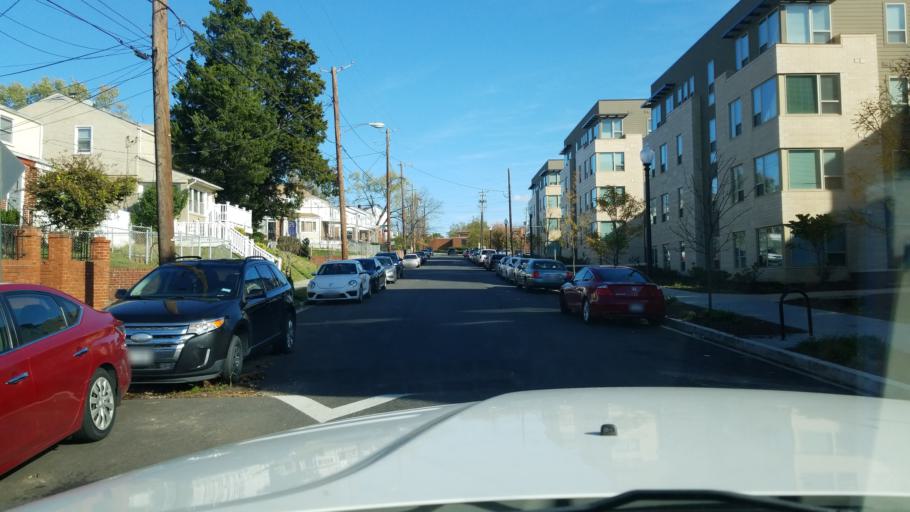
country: US
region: Maryland
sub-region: Prince George's County
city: Fairmount Heights
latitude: 38.8997
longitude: -76.9274
